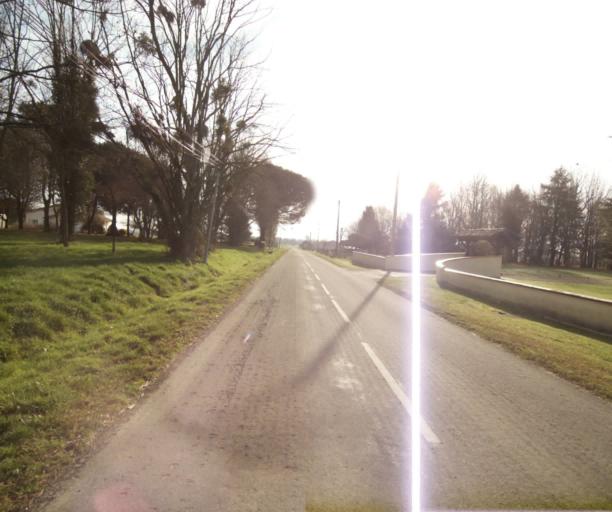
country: FR
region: Aquitaine
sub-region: Departement des Landes
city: Gabarret
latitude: 43.9848
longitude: 0.0228
